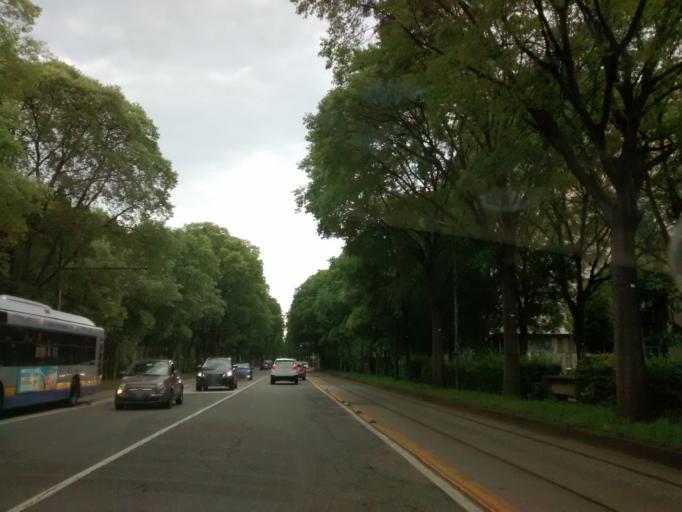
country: IT
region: Piedmont
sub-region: Provincia di Torino
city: Turin
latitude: 45.0621
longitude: 7.6624
